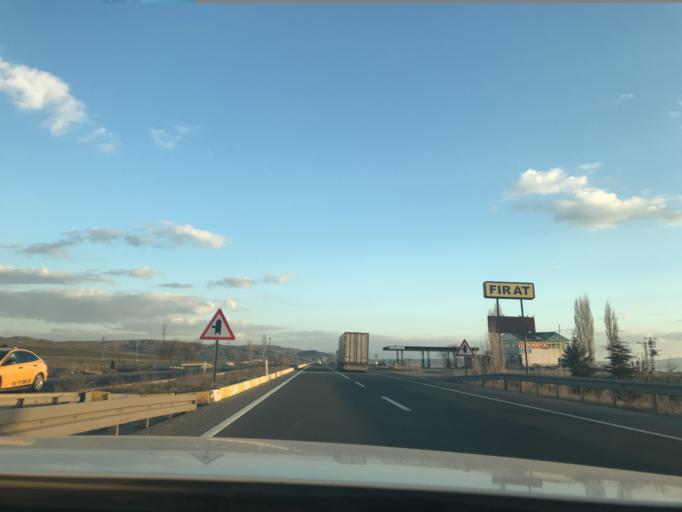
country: TR
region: Ankara
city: Altpinar
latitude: 39.3836
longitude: 32.8910
